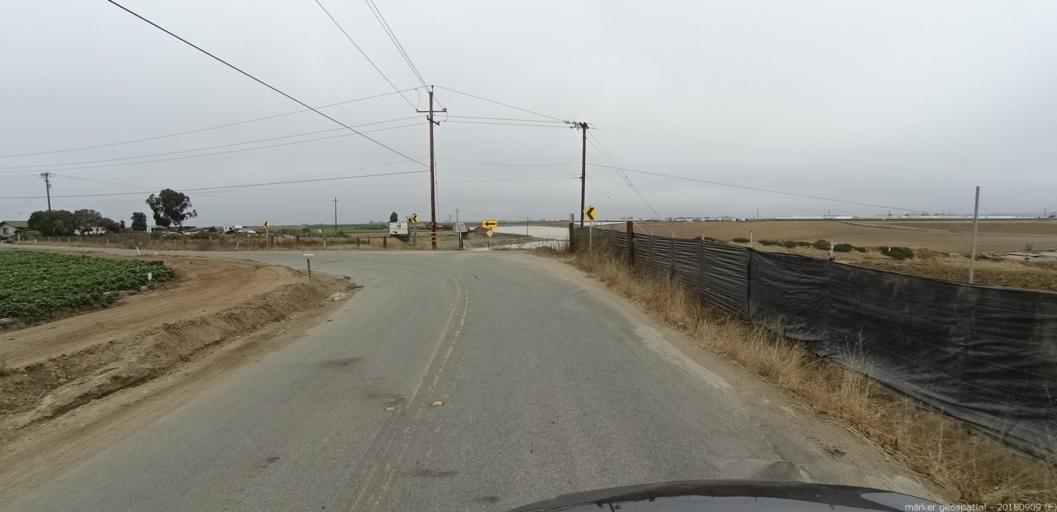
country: US
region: California
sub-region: Monterey County
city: Boronda
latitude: 36.7262
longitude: -121.6721
